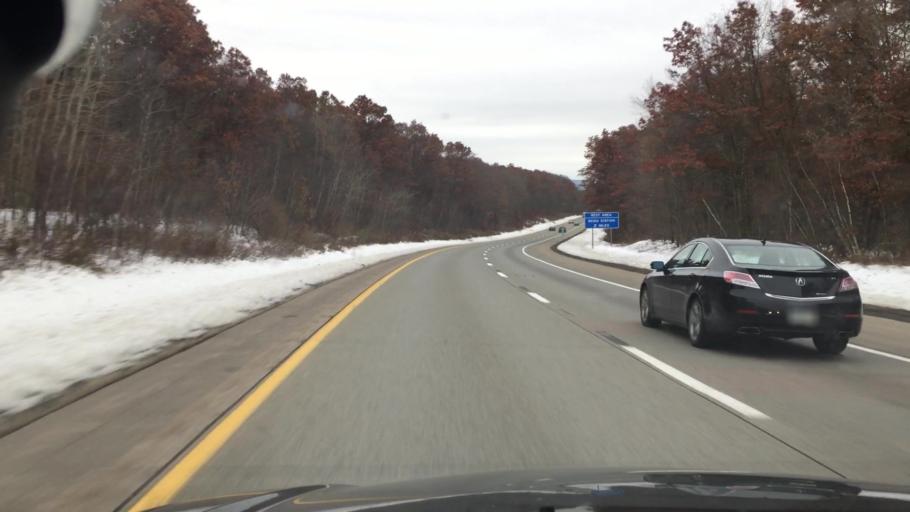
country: US
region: Pennsylvania
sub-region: Luzerne County
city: Nanticoke
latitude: 41.1607
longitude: -75.9560
